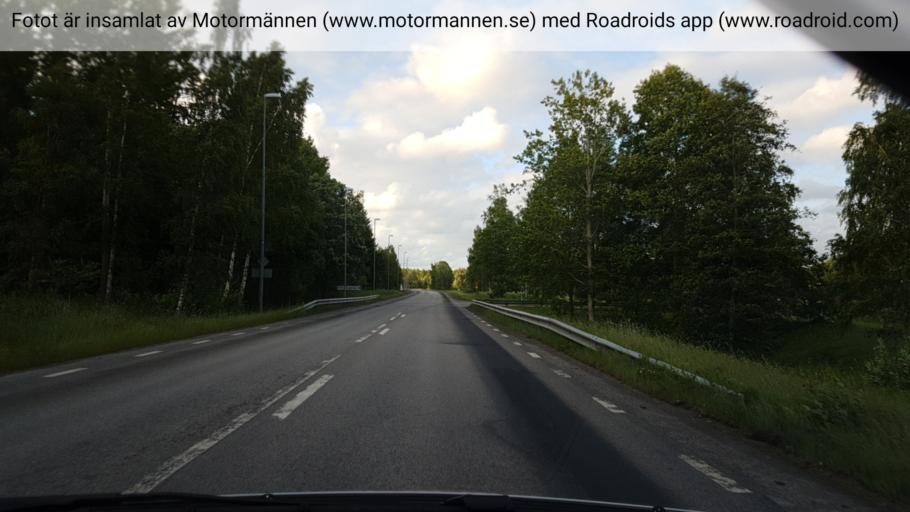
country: SE
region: OErebro
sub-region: Karlskoga Kommun
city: Karlskoga
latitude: 59.3405
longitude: 14.5760
